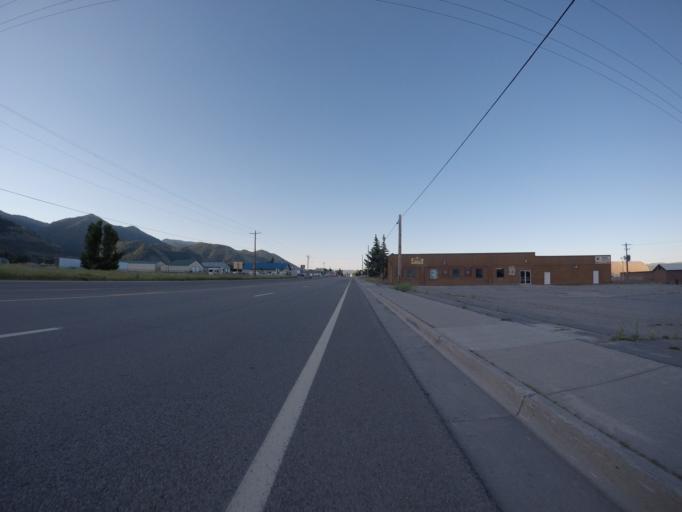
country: US
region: Wyoming
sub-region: Lincoln County
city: Afton
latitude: 42.7394
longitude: -110.9335
